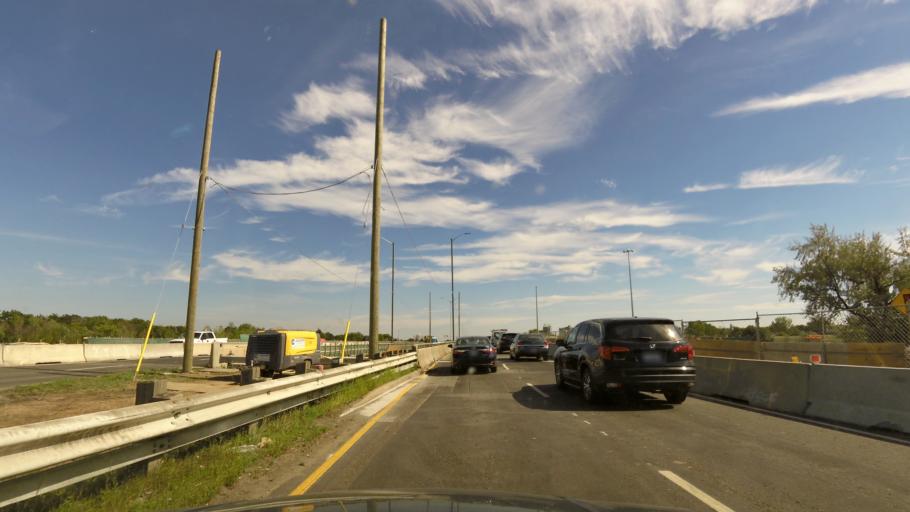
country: CA
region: Ontario
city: Mississauga
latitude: 43.5543
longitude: -79.6974
